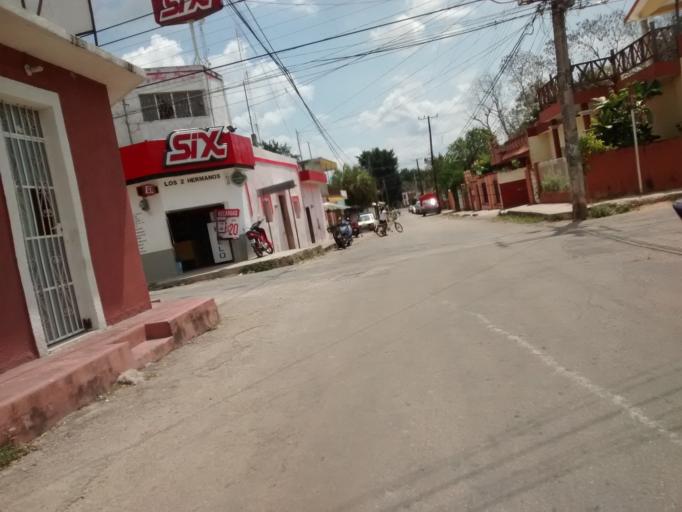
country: MX
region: Yucatan
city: Valladolid
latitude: 20.6856
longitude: -88.2128
